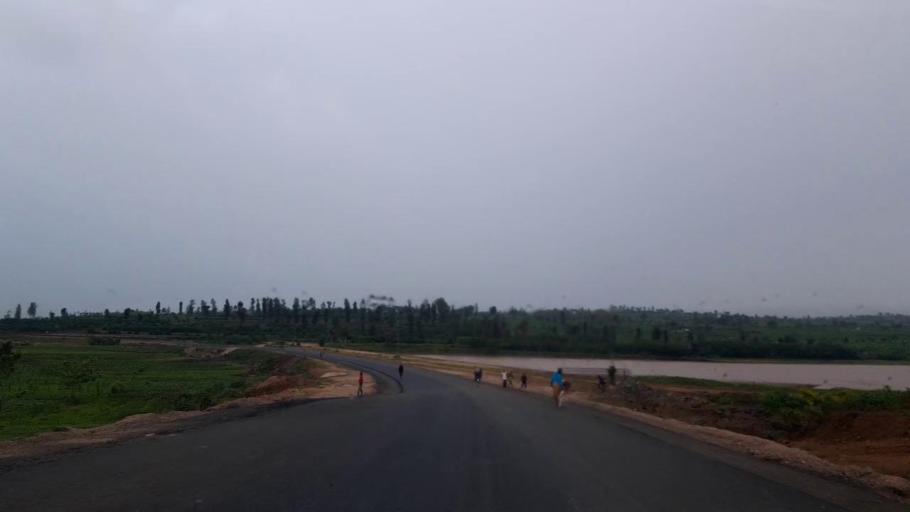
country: RW
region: Northern Province
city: Byumba
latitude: -1.4120
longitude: 30.2839
